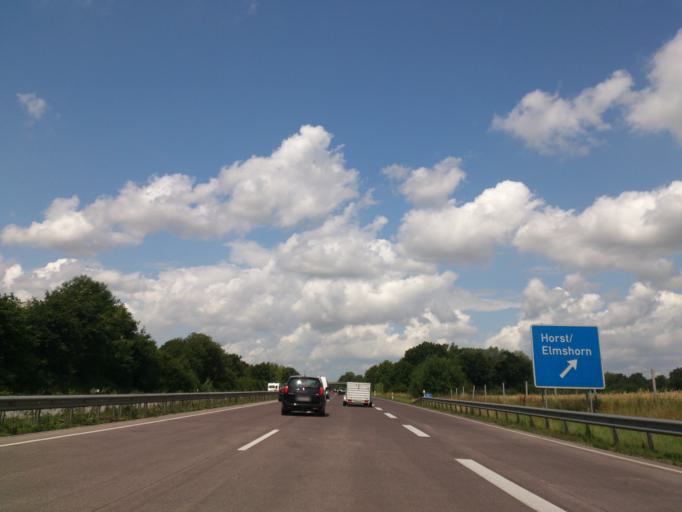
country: DE
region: Schleswig-Holstein
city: Klein Offenseth-Sparrieshoop
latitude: 53.8033
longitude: 9.6824
